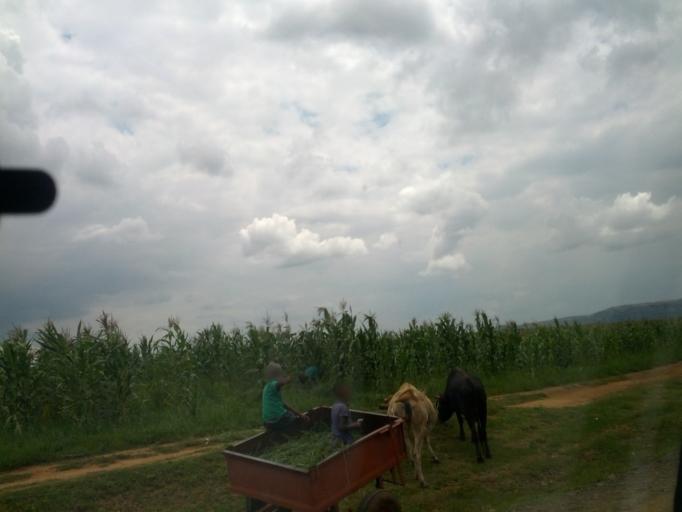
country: LS
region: Leribe
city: Leribe
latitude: -28.9342
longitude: 28.1534
